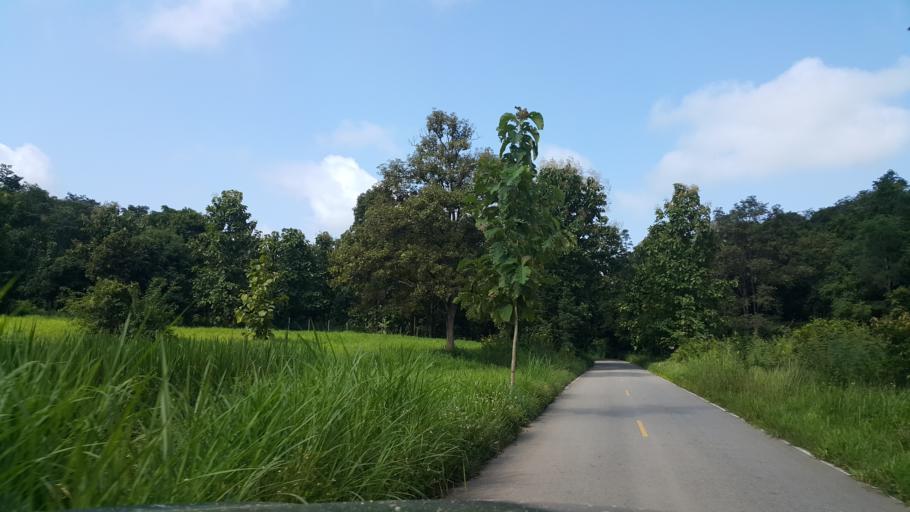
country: TH
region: Chiang Mai
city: Mae On
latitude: 18.7179
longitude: 99.2241
